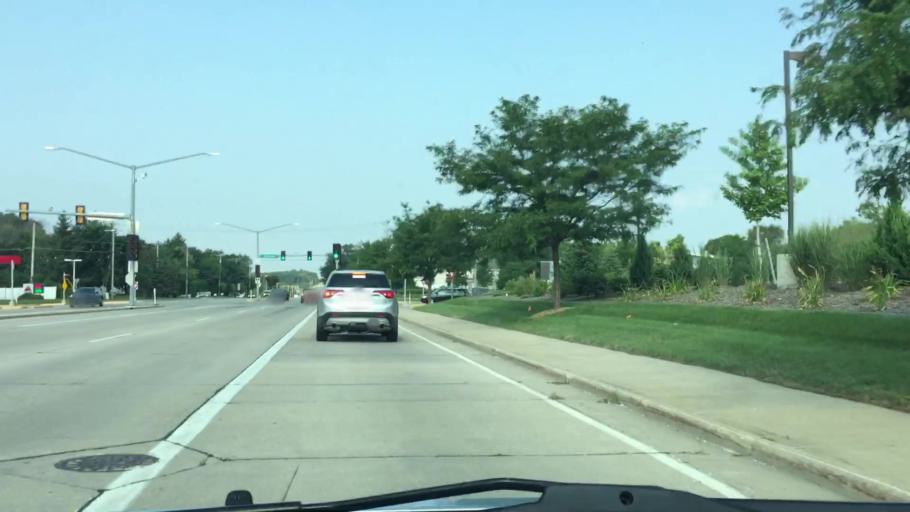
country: US
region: Wisconsin
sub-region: Waukesha County
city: New Berlin
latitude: 43.0170
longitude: -88.1259
